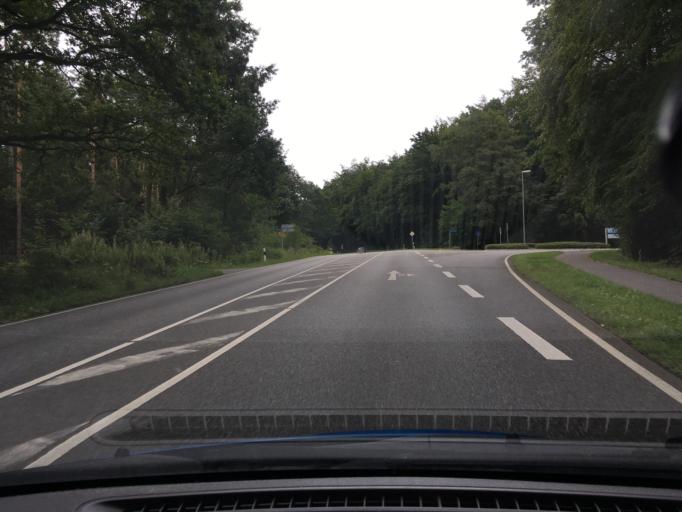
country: DE
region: Schleswig-Holstein
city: Wiershop
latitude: 53.4228
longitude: 10.4239
